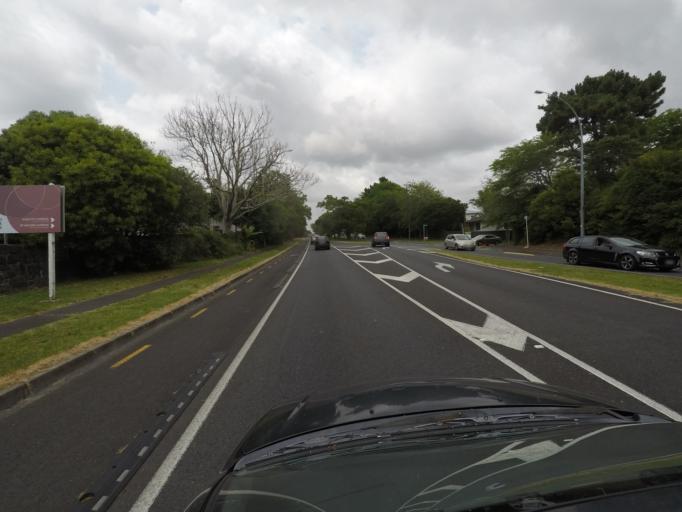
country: NZ
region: Auckland
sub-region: Auckland
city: Auckland
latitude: -36.8721
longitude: 174.7256
